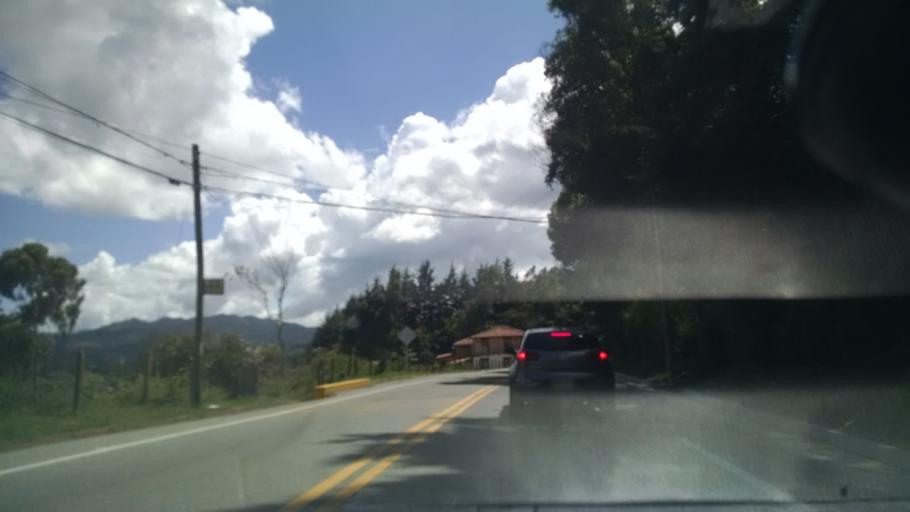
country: CO
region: Antioquia
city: El Retiro
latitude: 6.1240
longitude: -75.5011
